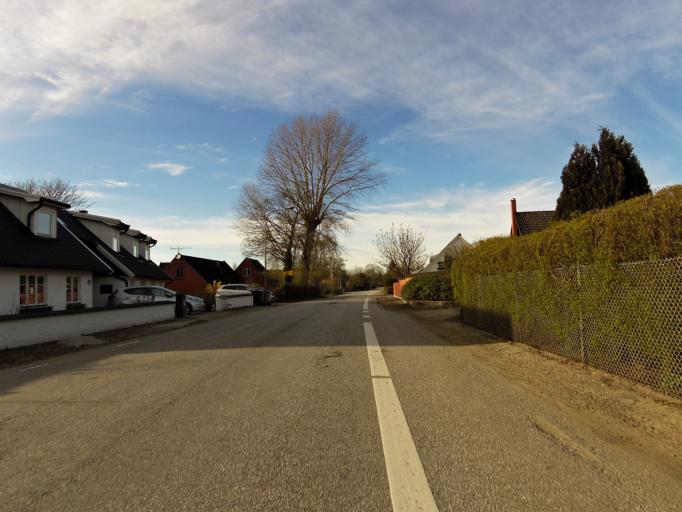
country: SE
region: Skane
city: Bjarred
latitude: 55.7305
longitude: 13.0323
